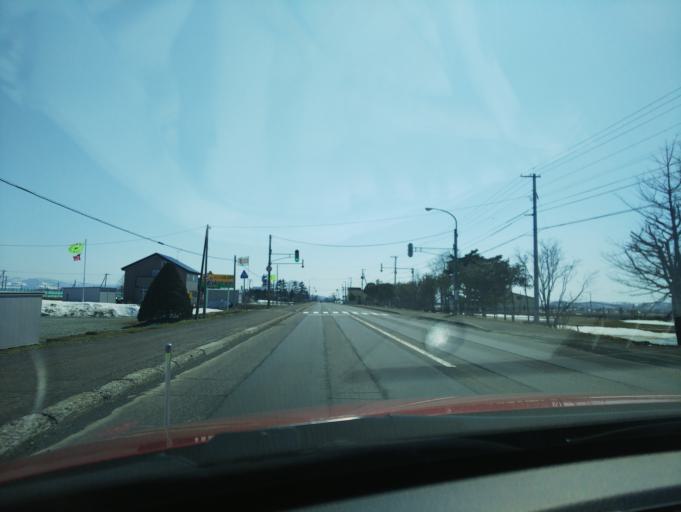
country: JP
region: Hokkaido
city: Nayoro
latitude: 44.2127
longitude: 142.3949
